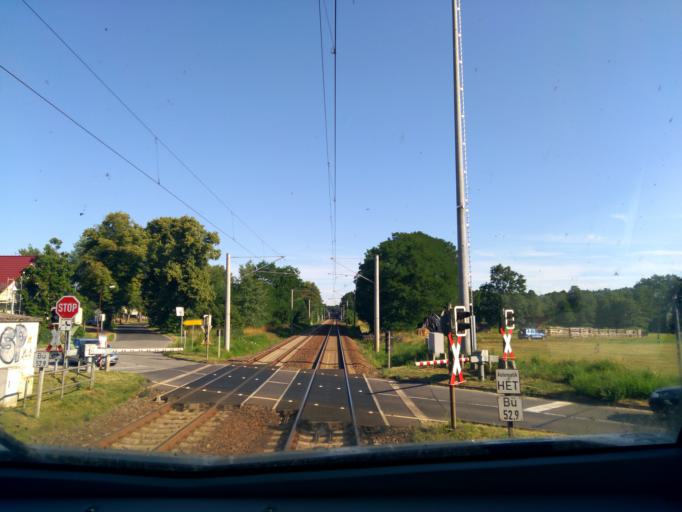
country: DE
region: Brandenburg
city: Halbe
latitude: 52.0896
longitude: 13.7201
